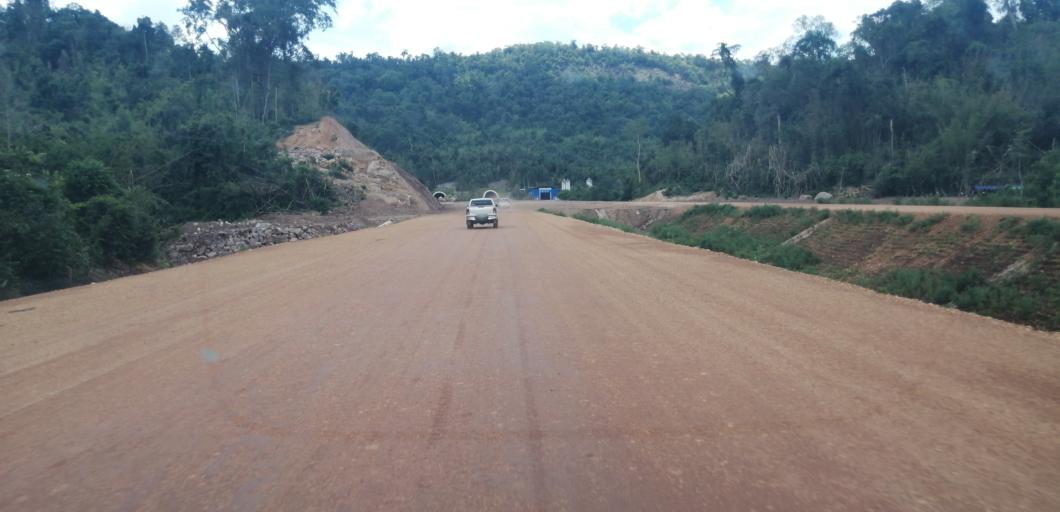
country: LA
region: Vientiane
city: Muang Phon-Hong
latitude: 18.5448
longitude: 102.3651
